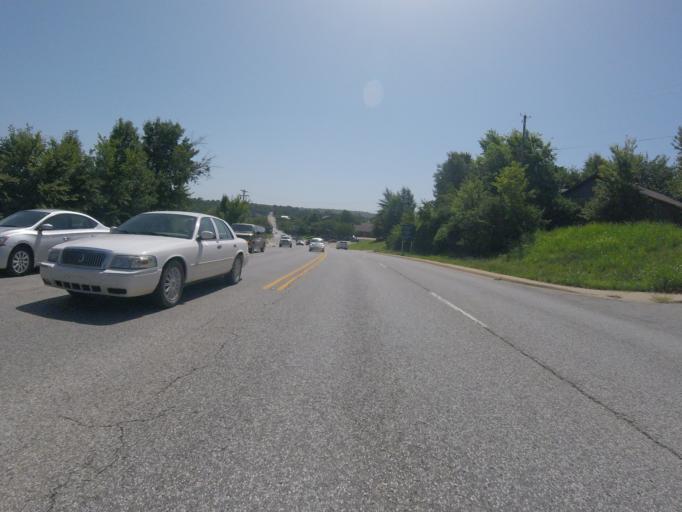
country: US
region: Arkansas
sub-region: Washington County
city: Fayetteville
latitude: 36.0777
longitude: -94.1772
